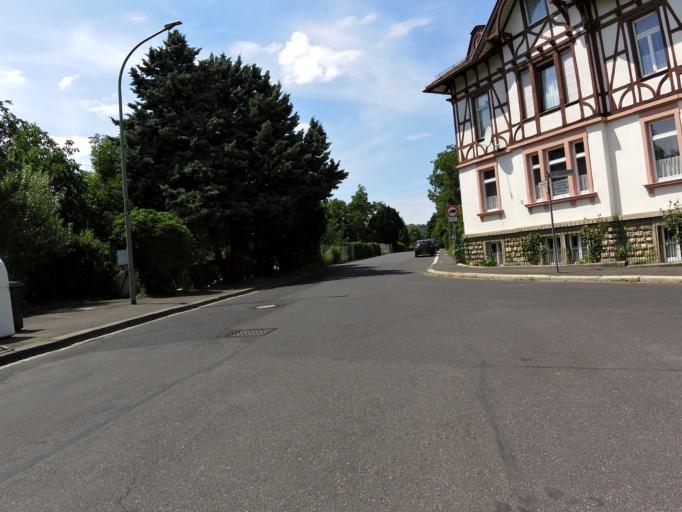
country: DE
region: Bavaria
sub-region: Regierungsbezirk Unterfranken
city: Randersacker
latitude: 49.7616
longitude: 9.9527
